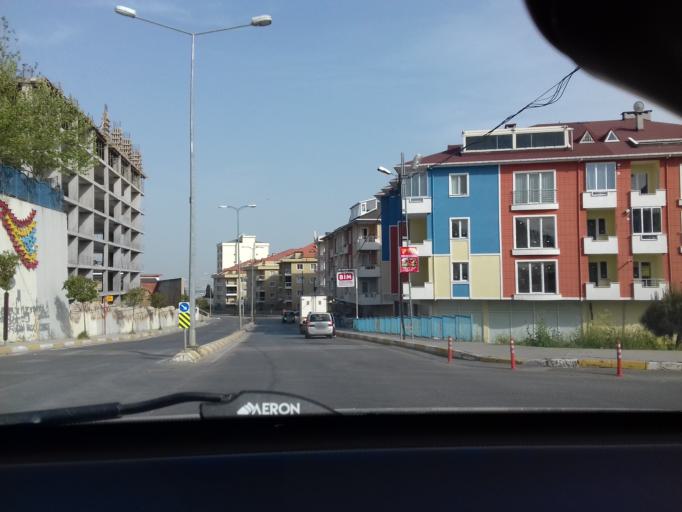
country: TR
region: Istanbul
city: Pendik
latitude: 40.9051
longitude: 29.2648
